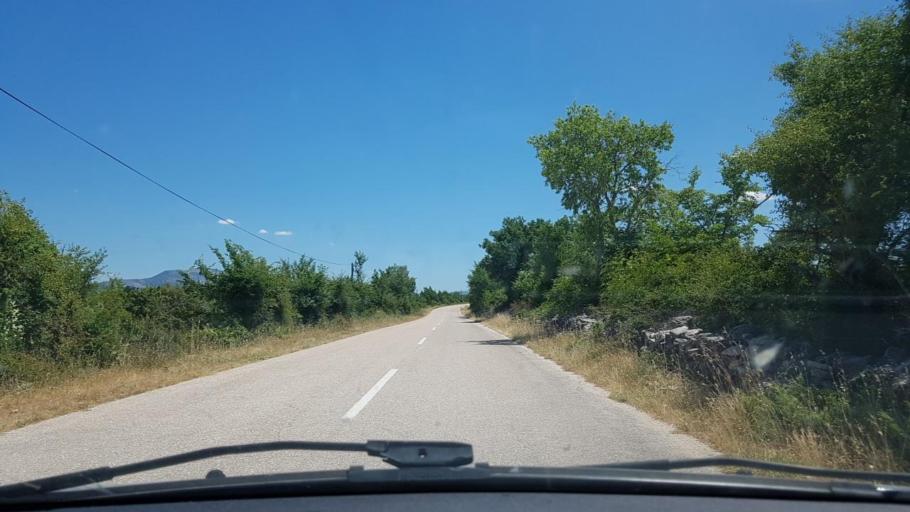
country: HR
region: Sibensko-Kniniska
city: Kistanje
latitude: 43.9732
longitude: 15.9710
